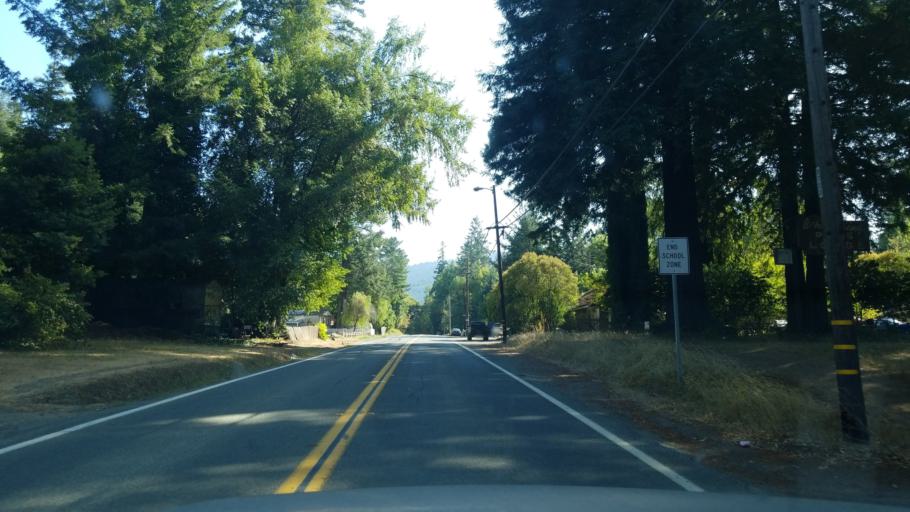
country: US
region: California
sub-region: Humboldt County
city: Redway
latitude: 40.2332
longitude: -123.8244
